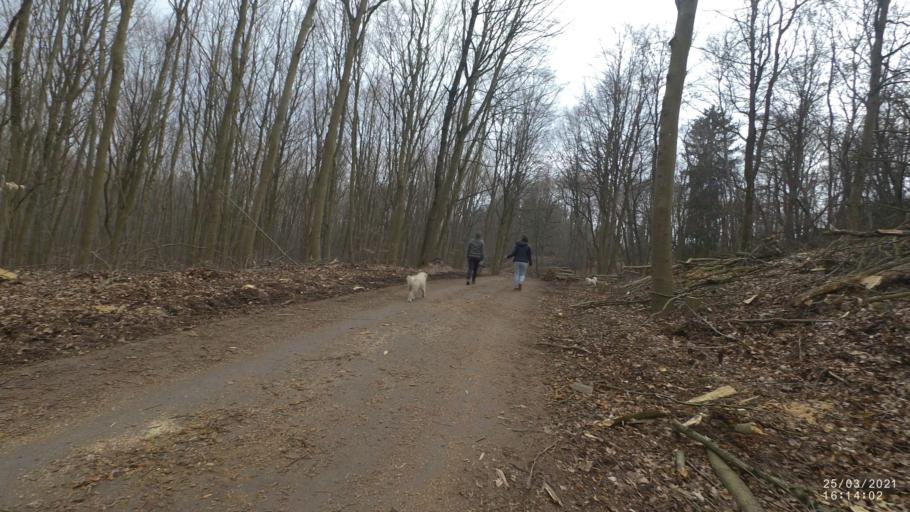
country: DE
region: Rheinland-Pfalz
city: Kottenheim
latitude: 50.3438
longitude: 7.2419
